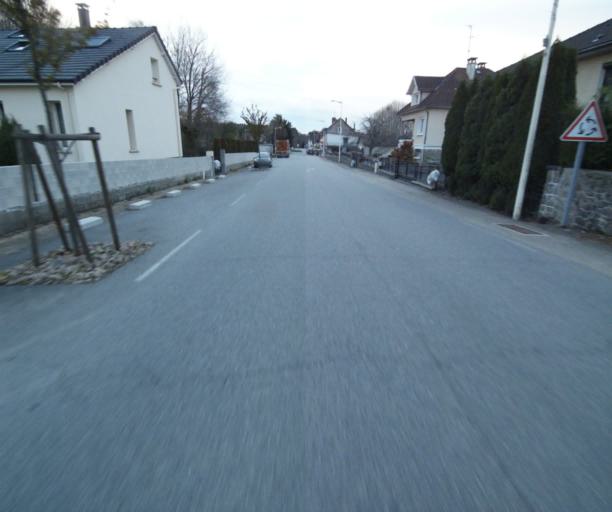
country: FR
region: Limousin
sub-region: Departement de la Correze
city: Correze
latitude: 45.3333
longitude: 1.8786
